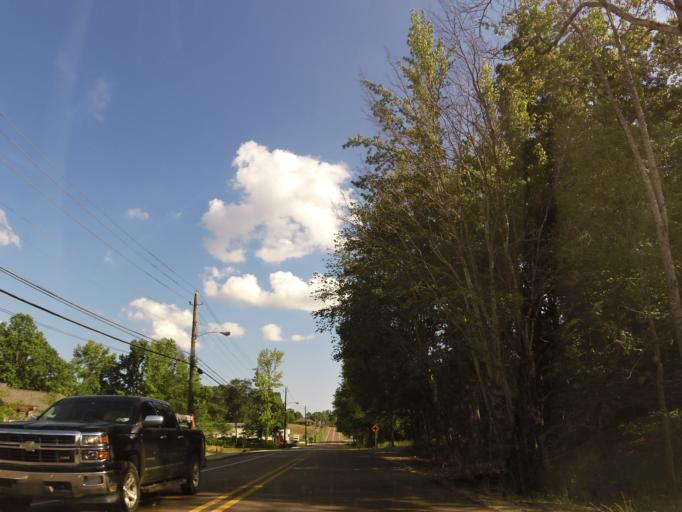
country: US
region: Mississippi
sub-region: Lafayette County
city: University
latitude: 34.3391
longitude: -89.5200
